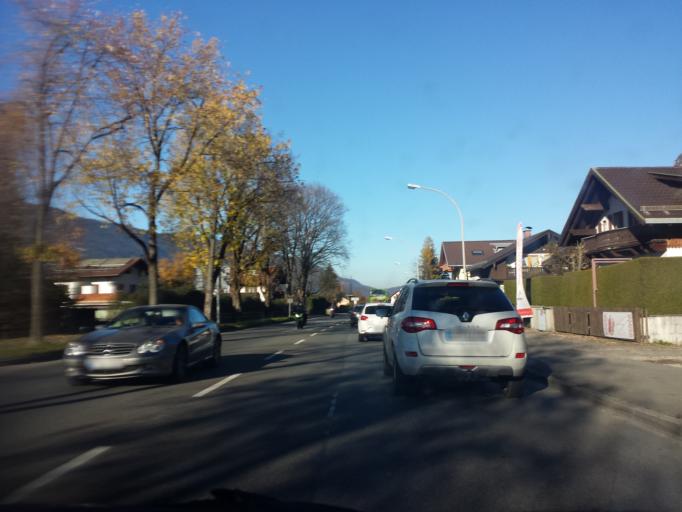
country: DE
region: Bavaria
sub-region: Upper Bavaria
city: Garmisch-Partenkirchen
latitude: 47.5058
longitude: 11.1038
